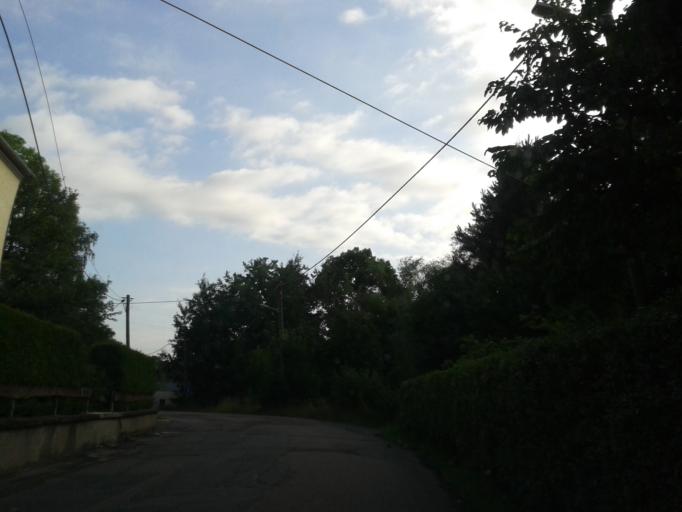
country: DE
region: Saxony
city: Halsbrucke
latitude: 50.9377
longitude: 13.3296
